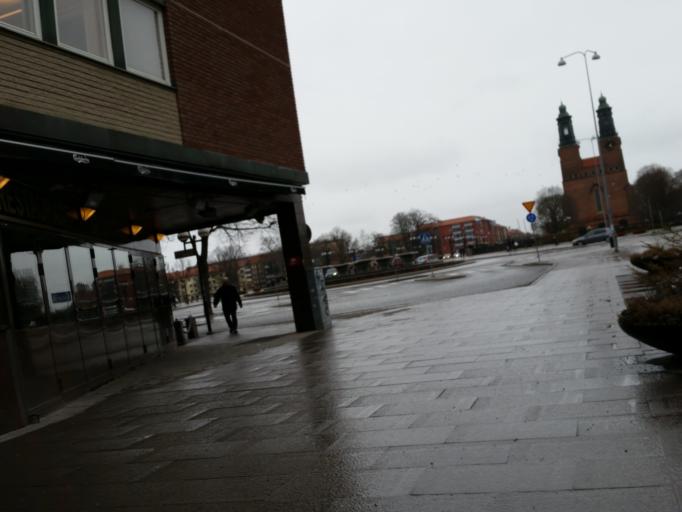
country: SE
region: Soedermanland
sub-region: Eskilstuna Kommun
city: Eskilstuna
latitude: 59.3720
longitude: 16.5151
